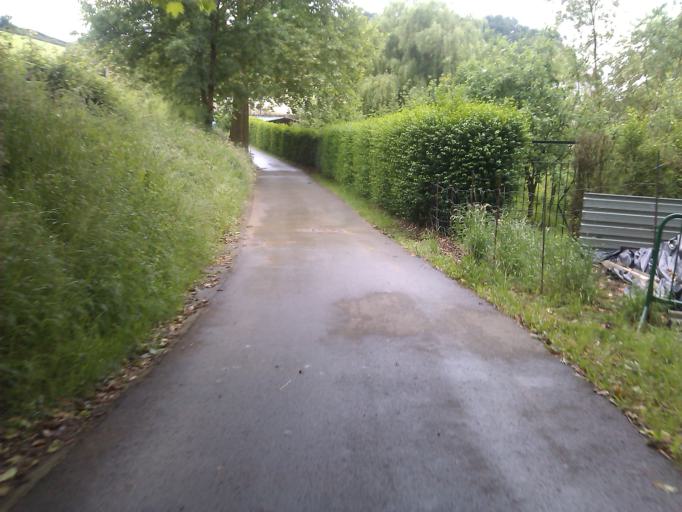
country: ES
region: Basque Country
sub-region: Provincia de Guipuzcoa
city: Urnieta
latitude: 43.2532
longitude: -1.9833
